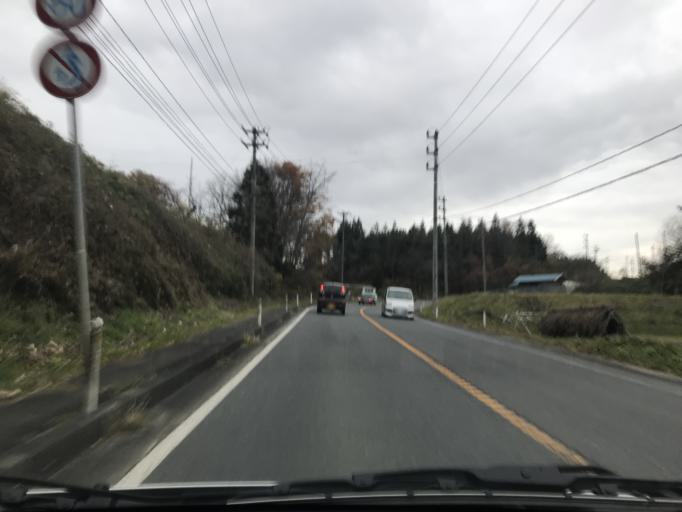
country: JP
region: Iwate
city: Ichinoseki
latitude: 39.0130
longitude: 141.3285
